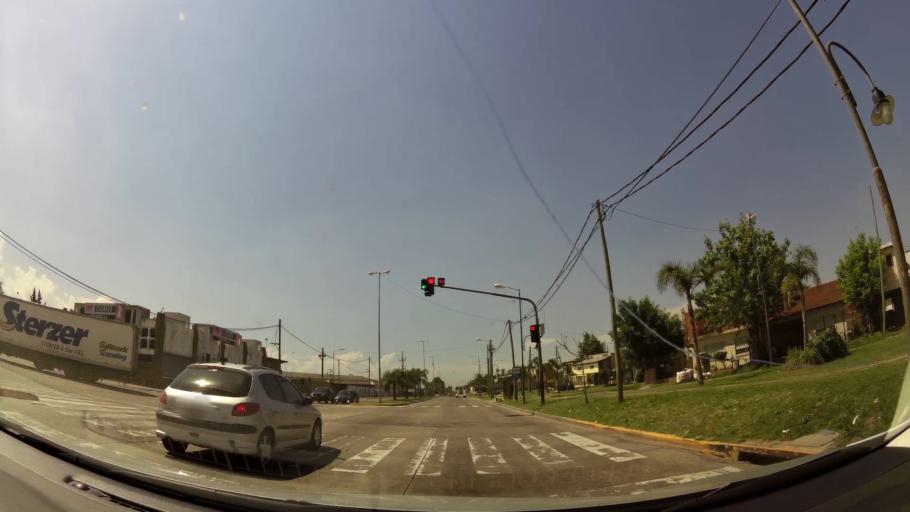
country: AR
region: Buenos Aires
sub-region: Partido de Tigre
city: Tigre
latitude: -34.4693
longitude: -58.5964
